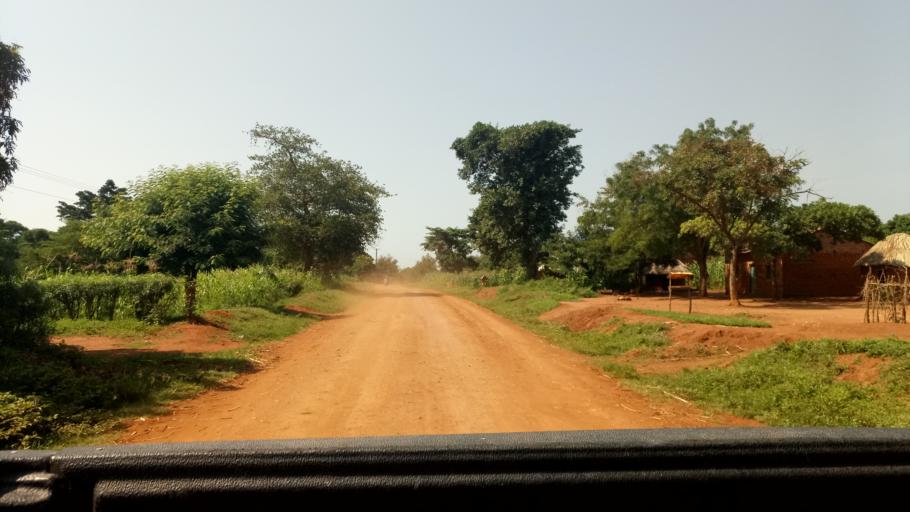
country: UG
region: Eastern Region
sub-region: Kaliro District
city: Kaliro
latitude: 0.9633
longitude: 33.4690
